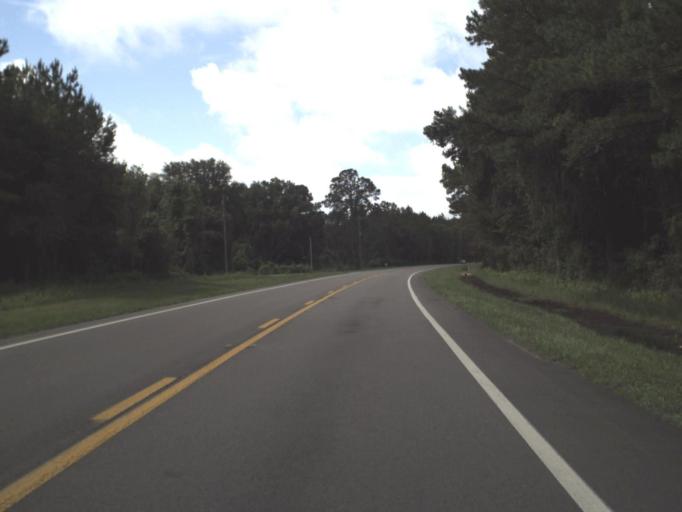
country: US
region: Florida
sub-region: Columbia County
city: Five Points
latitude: 30.2814
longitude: -82.6306
